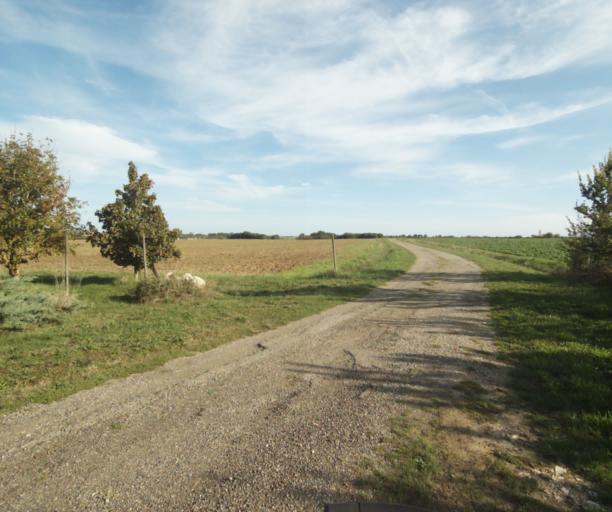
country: FR
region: Midi-Pyrenees
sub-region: Departement du Tarn-et-Garonne
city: Saint-Porquier
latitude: 43.9286
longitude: 1.1345
